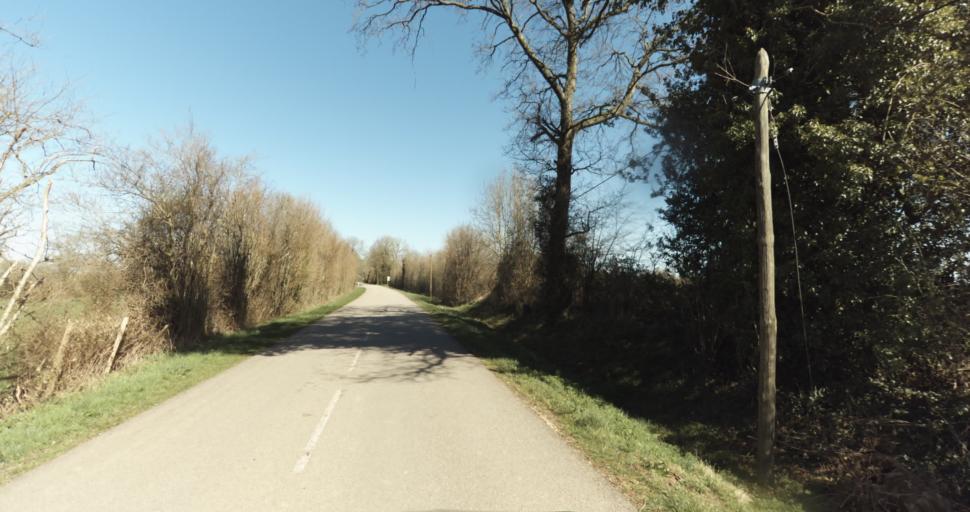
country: FR
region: Lower Normandy
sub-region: Departement de l'Orne
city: Trun
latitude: 48.9185
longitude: 0.0642
